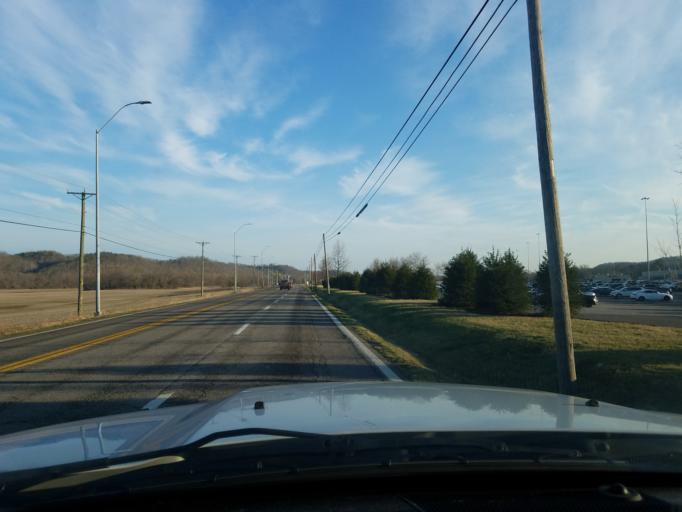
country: US
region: West Virginia
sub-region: Putnam County
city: Buffalo
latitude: 38.5958
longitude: -81.9966
